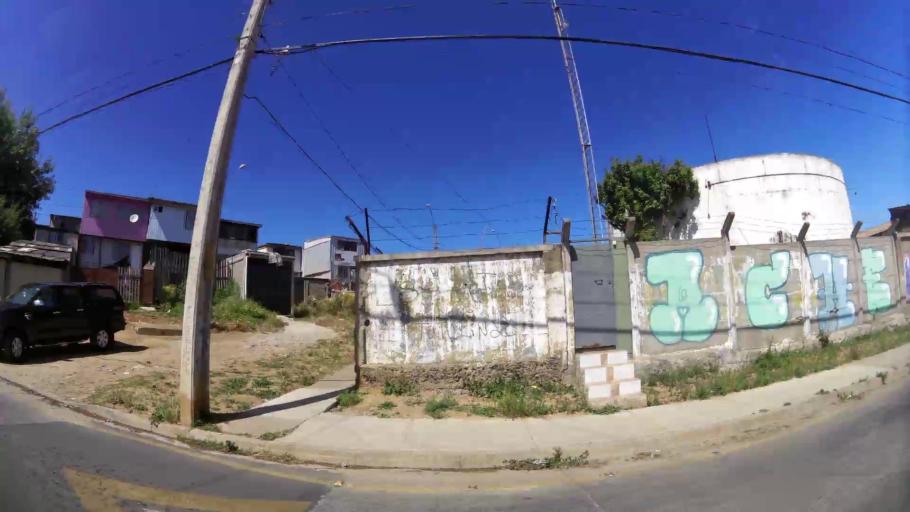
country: CL
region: Valparaiso
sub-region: Provincia de Valparaiso
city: Valparaiso
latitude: -33.0453
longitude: -71.6479
